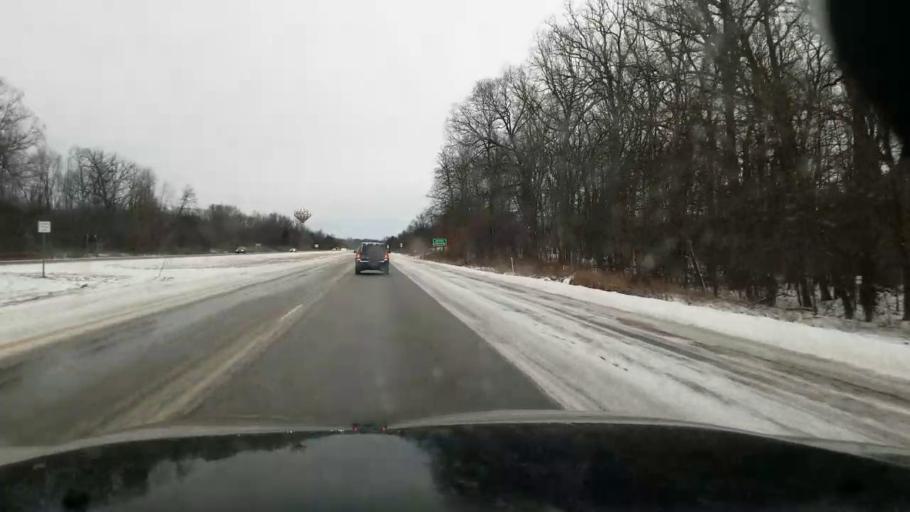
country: US
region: Michigan
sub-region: Jackson County
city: Jackson
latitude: 42.2478
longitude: -84.4761
